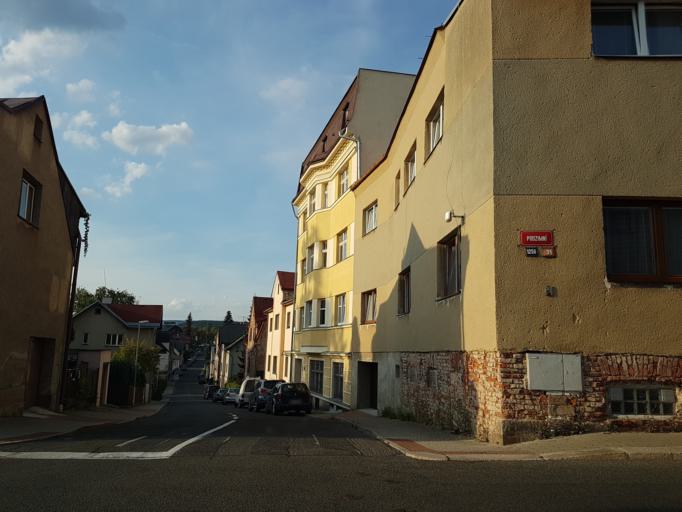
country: CZ
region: Liberecky
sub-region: Okres Jablonec nad Nisou
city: Jablonec nad Nisou
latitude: 50.7272
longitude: 15.1789
